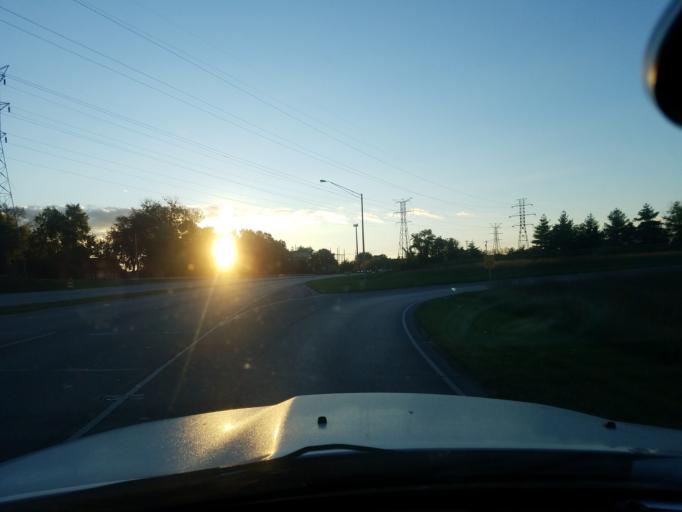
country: US
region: Indiana
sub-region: Clark County
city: Clarksville
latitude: 38.3027
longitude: -85.7813
